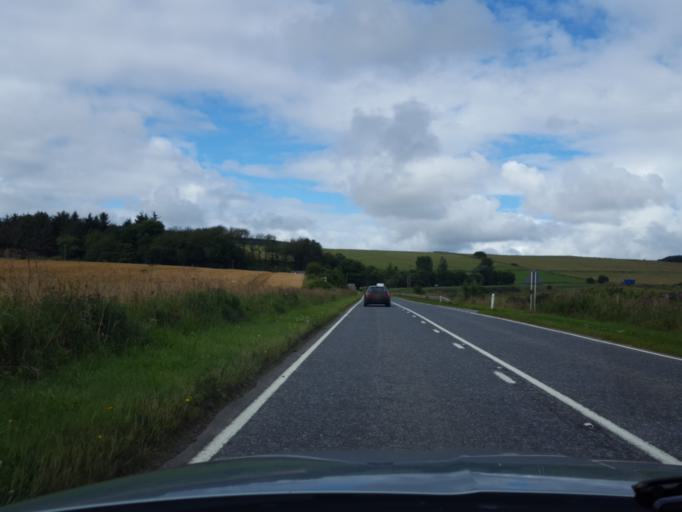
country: GB
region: Scotland
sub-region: Moray
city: Rothes
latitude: 57.5350
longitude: -3.2146
